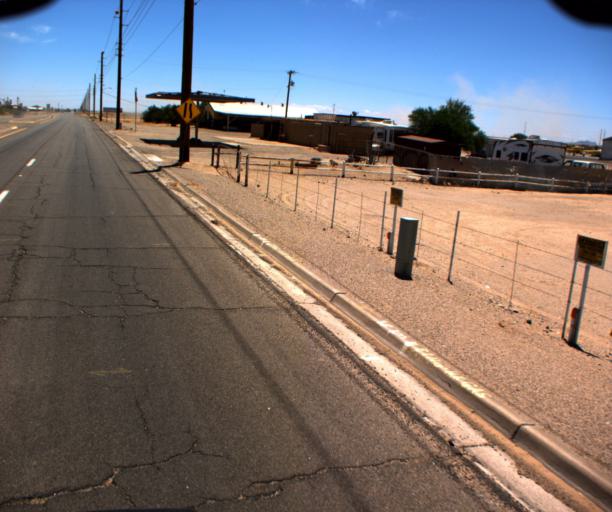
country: US
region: Arizona
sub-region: Pinal County
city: Maricopa
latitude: 32.8793
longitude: -111.9593
